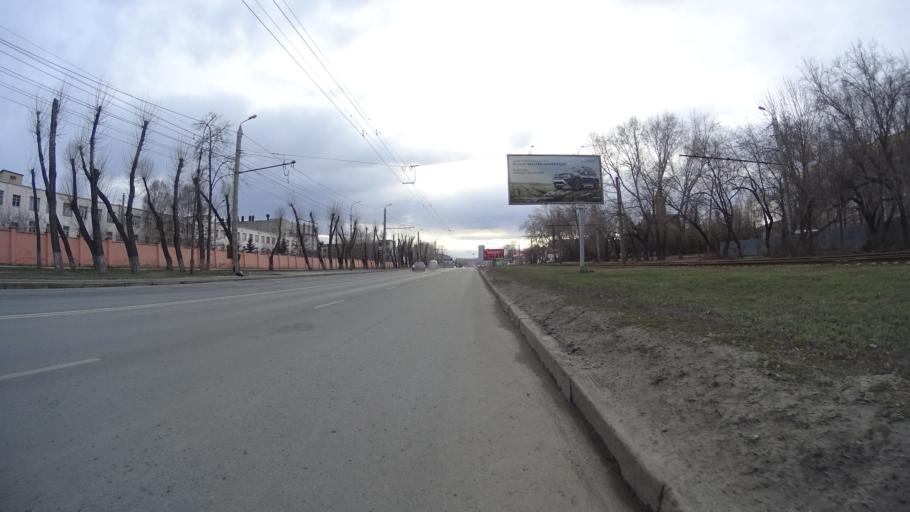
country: RU
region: Chelyabinsk
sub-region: Gorod Chelyabinsk
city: Chelyabinsk
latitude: 55.1598
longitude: 61.4572
